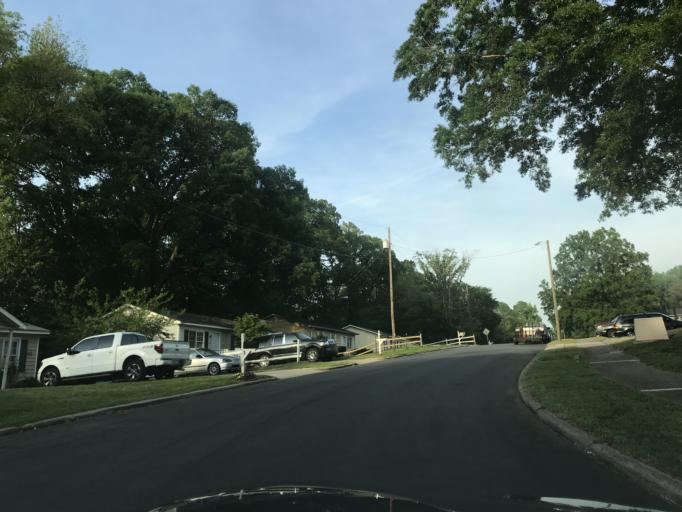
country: US
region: North Carolina
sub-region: Wake County
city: Raleigh
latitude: 35.7446
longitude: -78.6542
